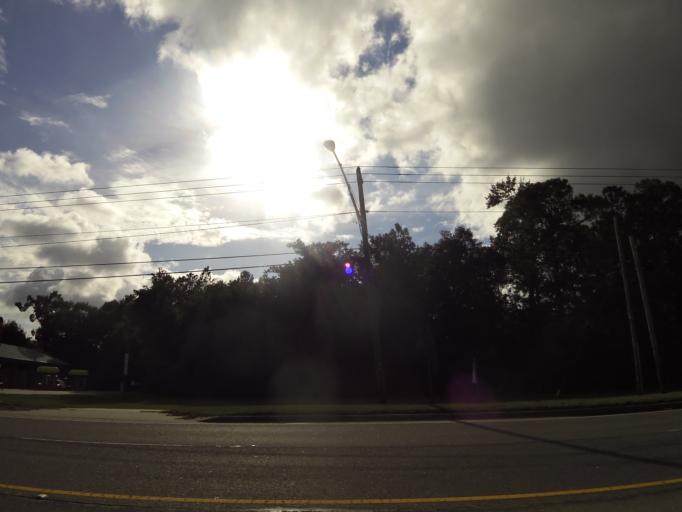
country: US
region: Georgia
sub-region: Liberty County
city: Hinesville
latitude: 31.8495
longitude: -81.6059
